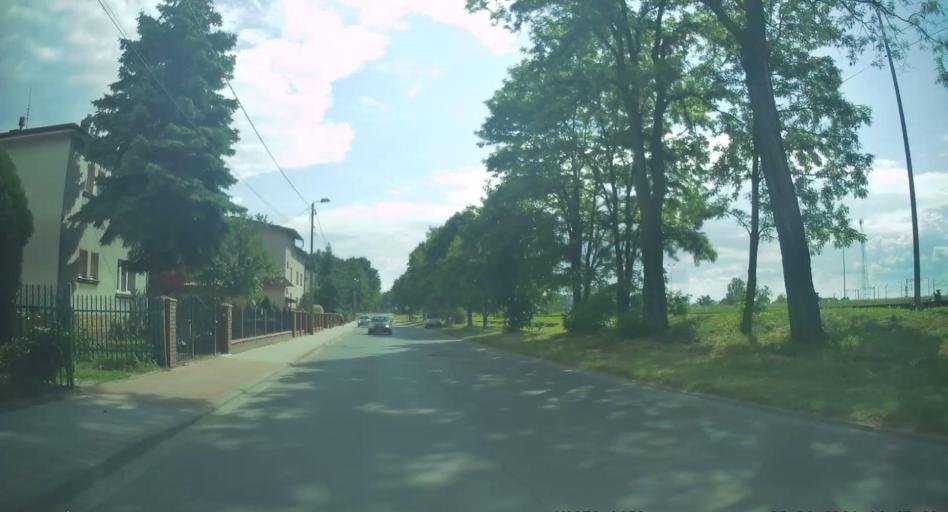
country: PL
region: Subcarpathian Voivodeship
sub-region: Powiat debicki
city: Debica
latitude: 50.0494
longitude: 21.3950
